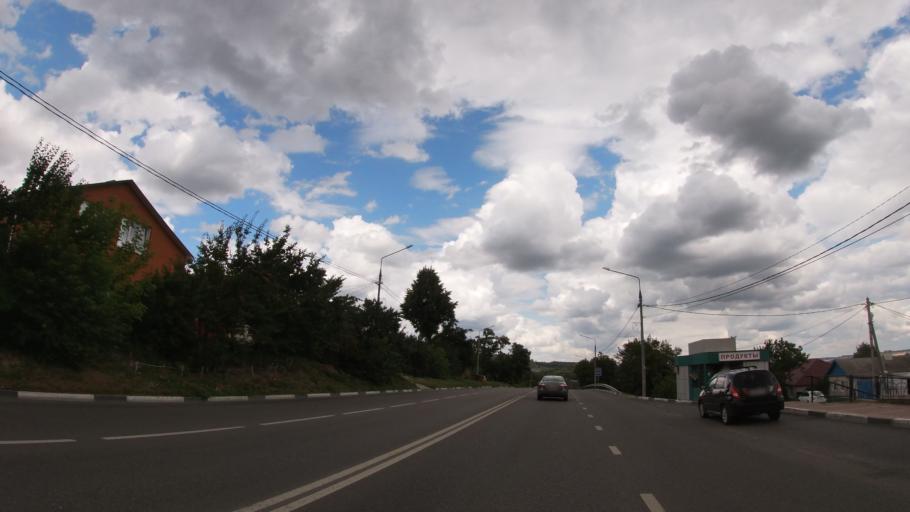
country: RU
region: Belgorod
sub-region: Belgorodskiy Rayon
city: Belgorod
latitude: 50.6034
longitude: 36.6101
